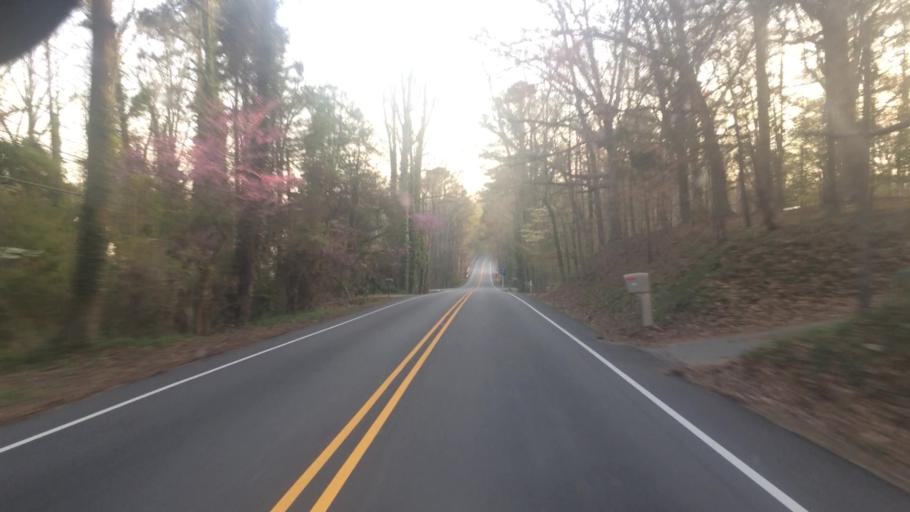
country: US
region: Virginia
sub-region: James City County
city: Williamsburg
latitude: 37.2409
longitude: -76.7445
